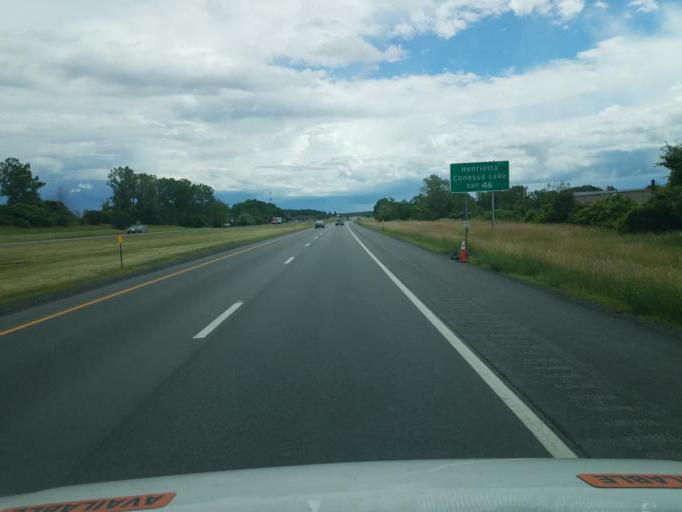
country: US
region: New York
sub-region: Monroe County
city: Scottsville
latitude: 43.0467
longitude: -77.6685
